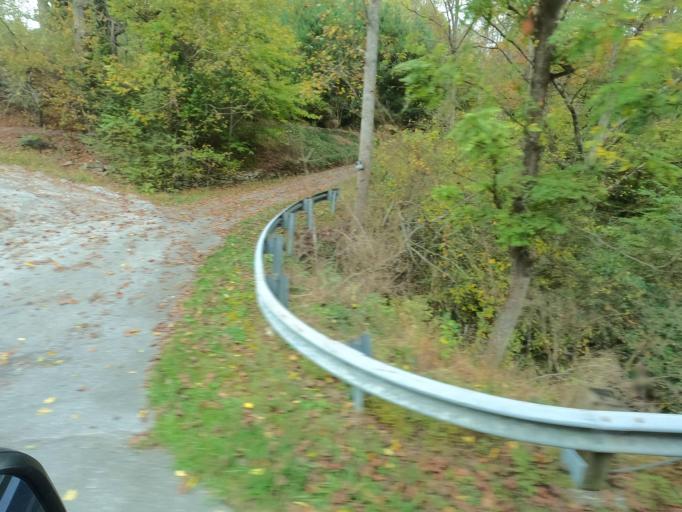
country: US
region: Tennessee
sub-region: Carter County
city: Roan Mountain
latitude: 36.2217
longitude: -82.1781
